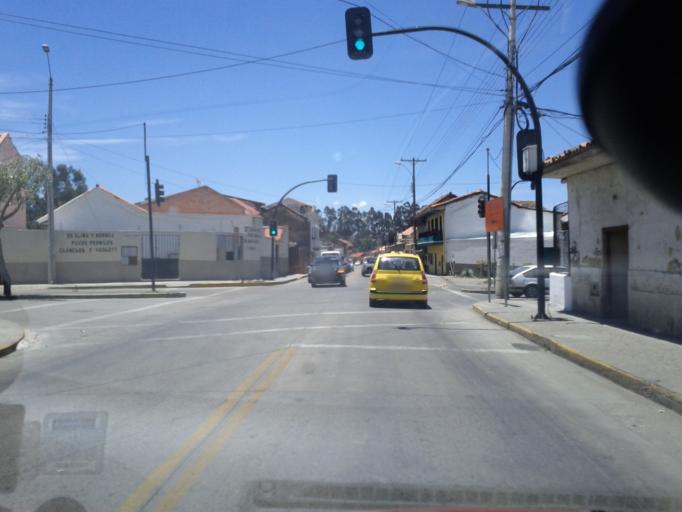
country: EC
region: Azuay
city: Cuenca
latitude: -2.9101
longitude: -79.0283
